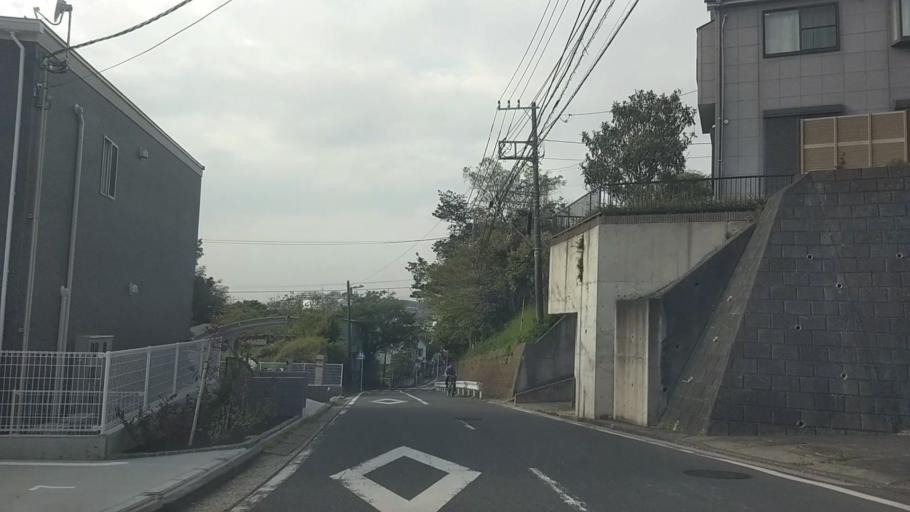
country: JP
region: Kanagawa
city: Kamakura
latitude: 35.3615
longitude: 139.5574
